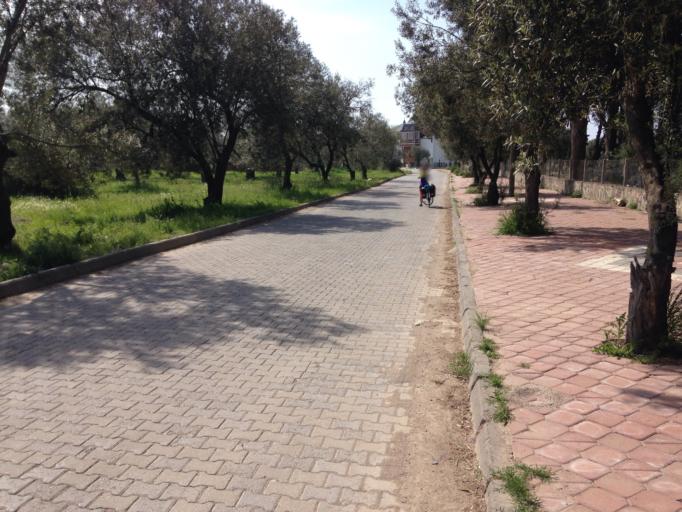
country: TR
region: Izmir
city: Dikili
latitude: 39.0822
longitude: 26.8970
